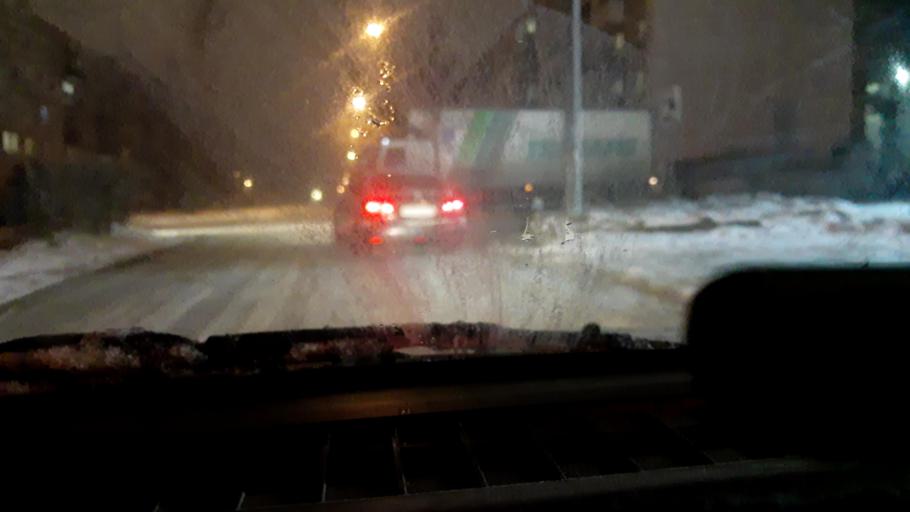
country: RU
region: Nizjnij Novgorod
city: Kstovo
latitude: 56.1483
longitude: 44.1825
